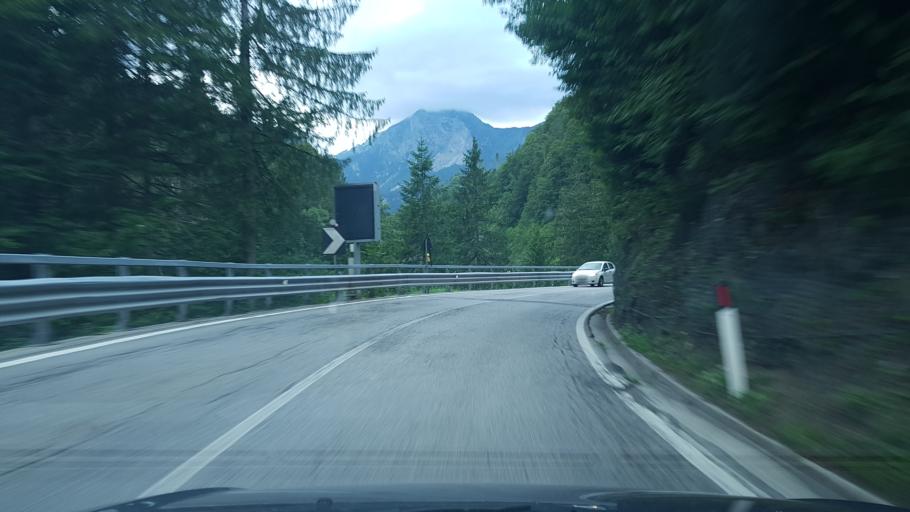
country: IT
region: Friuli Venezia Giulia
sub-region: Provincia di Udine
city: Forni Avoltri
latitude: 46.5703
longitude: 12.8105
